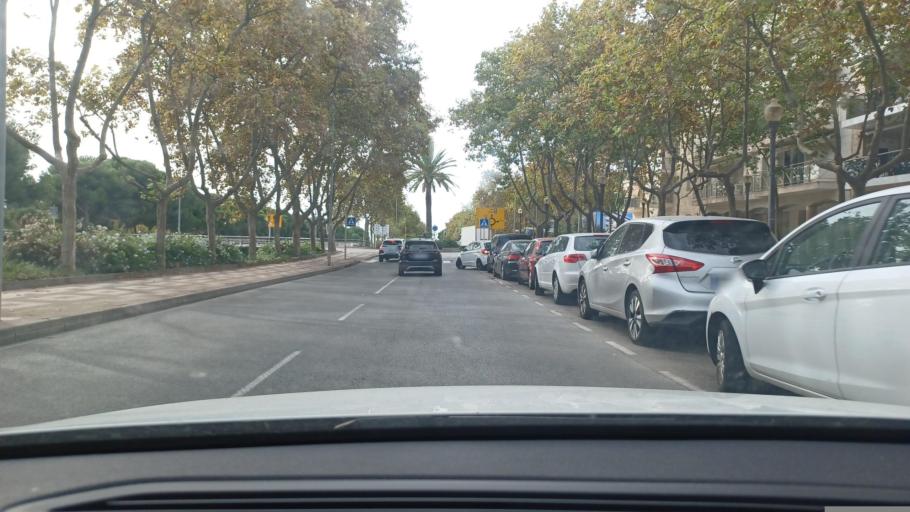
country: ES
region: Catalonia
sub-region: Provincia de Tarragona
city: Cambrils
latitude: 41.0678
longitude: 1.0556
